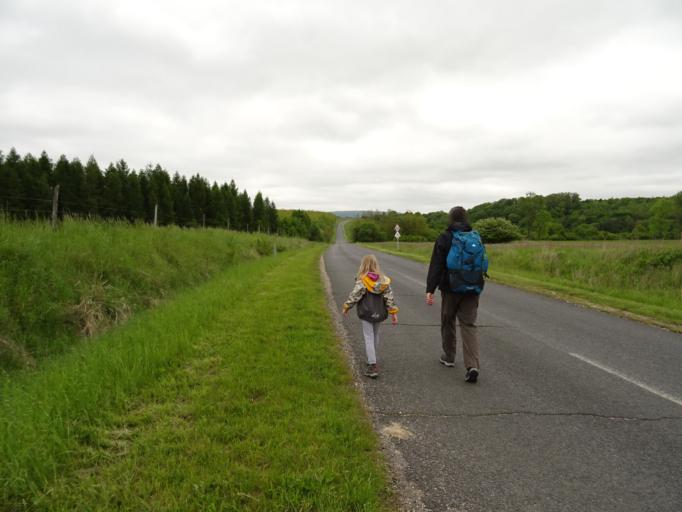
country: HU
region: Veszprem
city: Urkut
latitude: 47.1579
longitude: 17.6682
